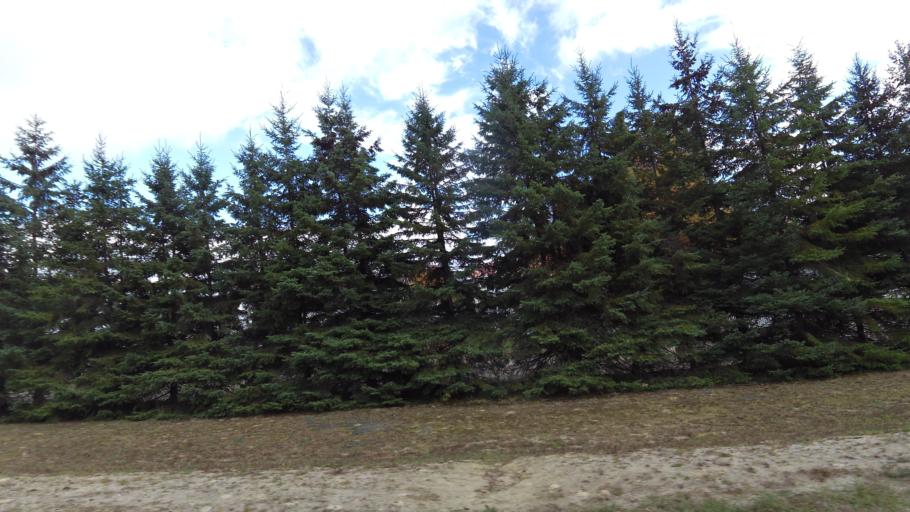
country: CA
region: Ontario
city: Deep River
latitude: 46.0954
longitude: -77.4849
